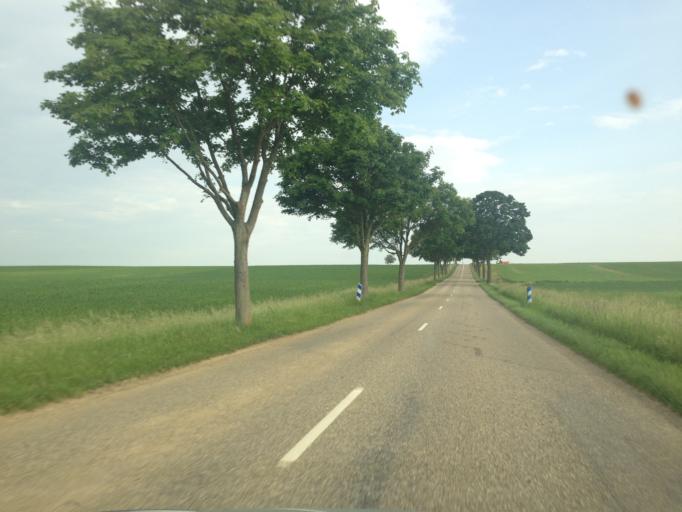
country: FR
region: Alsace
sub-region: Departement du Bas-Rhin
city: Schwindratzheim
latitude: 48.7732
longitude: 7.5941
